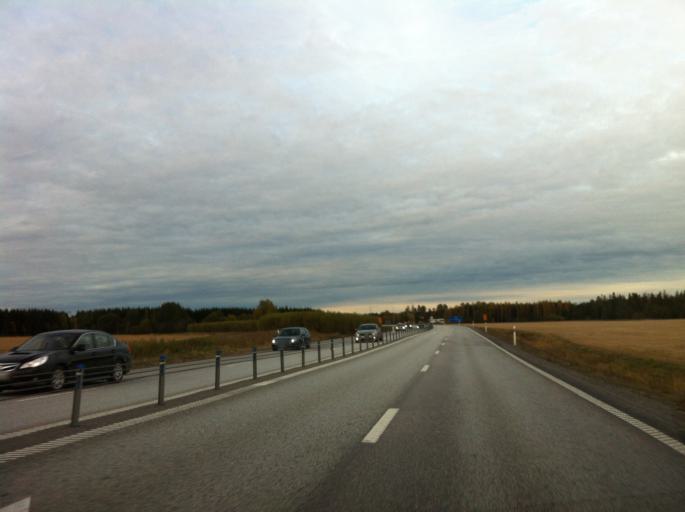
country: SE
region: OErebro
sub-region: Orebro Kommun
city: Hovsta
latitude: 59.4037
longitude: 15.1860
